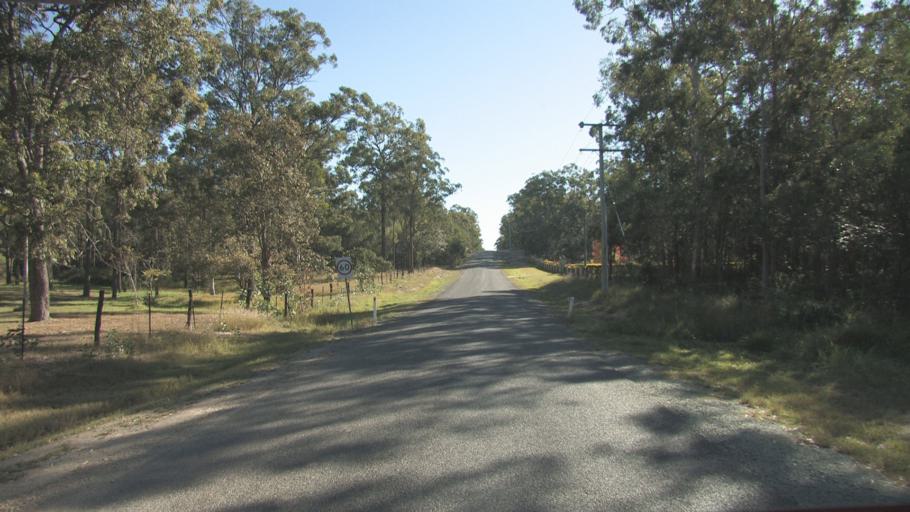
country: AU
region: Queensland
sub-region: Logan
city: Logan Reserve
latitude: -27.7636
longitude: 153.1388
